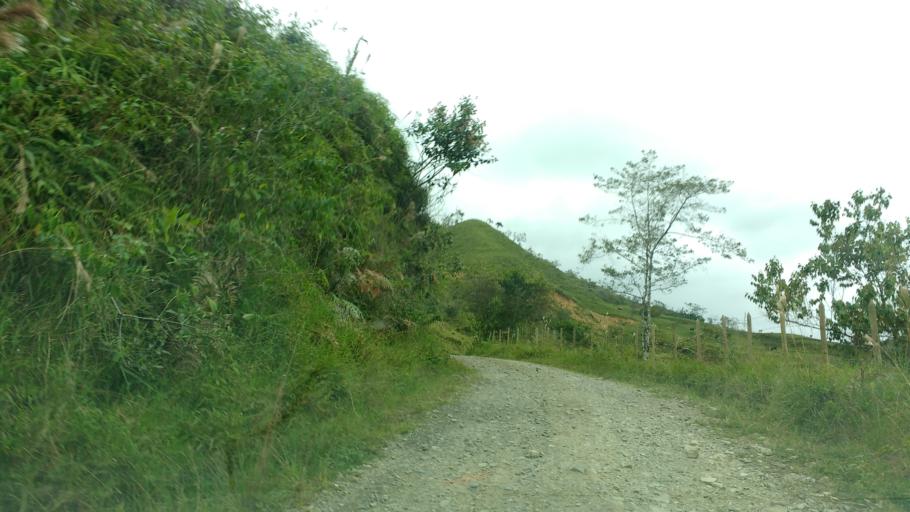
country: CO
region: Antioquia
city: Concepcion
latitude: 6.3762
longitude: -75.2294
